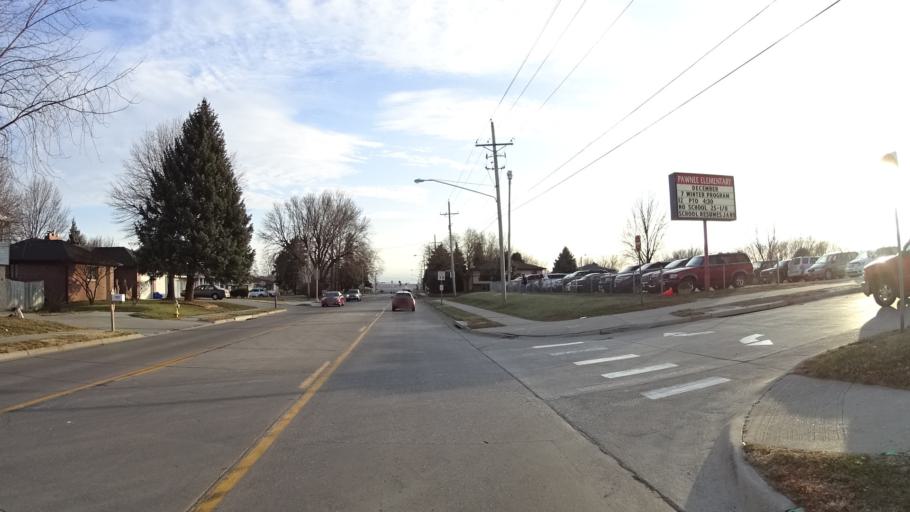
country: US
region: Nebraska
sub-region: Sarpy County
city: La Vista
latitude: 41.1856
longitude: -95.9867
